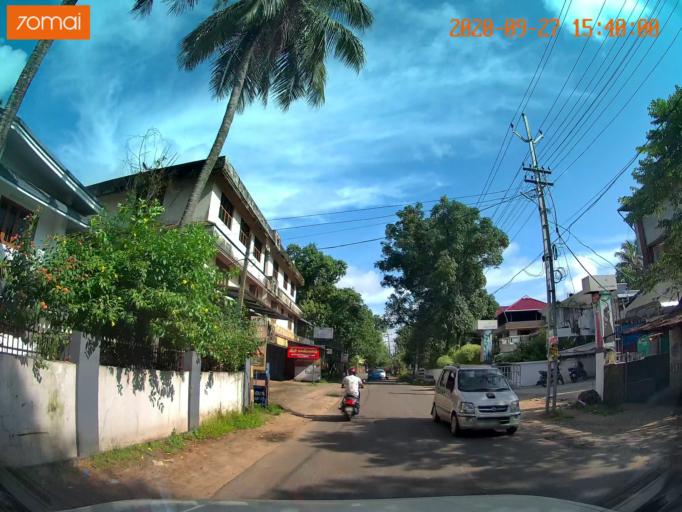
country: IN
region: Kerala
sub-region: Thrissur District
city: Thanniyam
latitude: 10.4696
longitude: 76.0841
